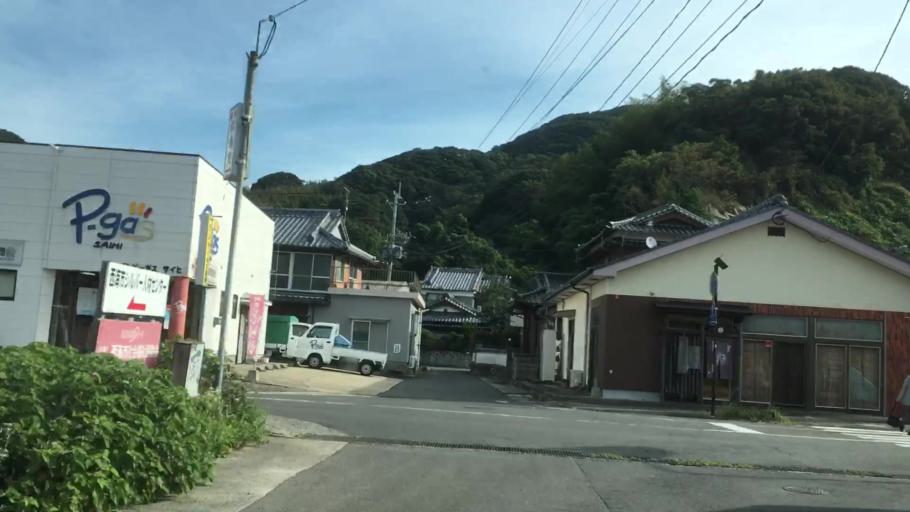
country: JP
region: Nagasaki
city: Sasebo
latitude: 32.9448
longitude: 129.6385
